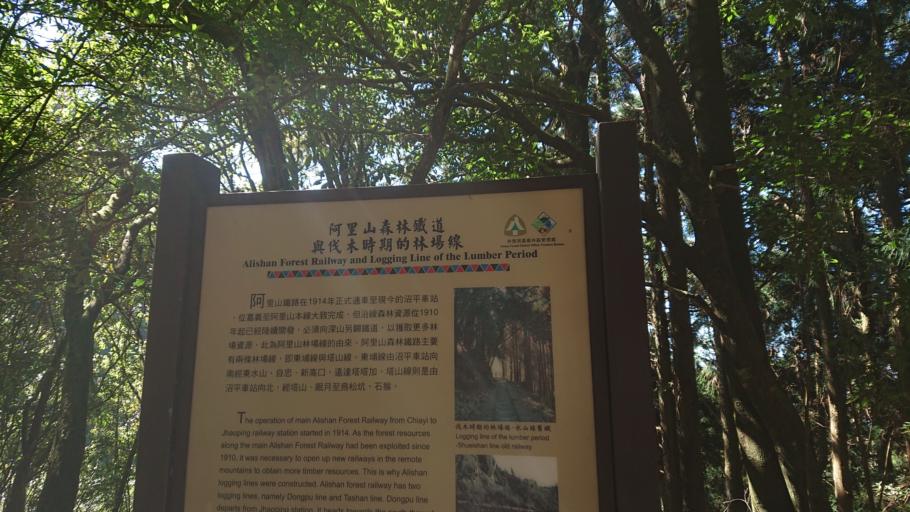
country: TW
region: Taiwan
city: Lugu
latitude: 23.4808
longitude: 120.8244
